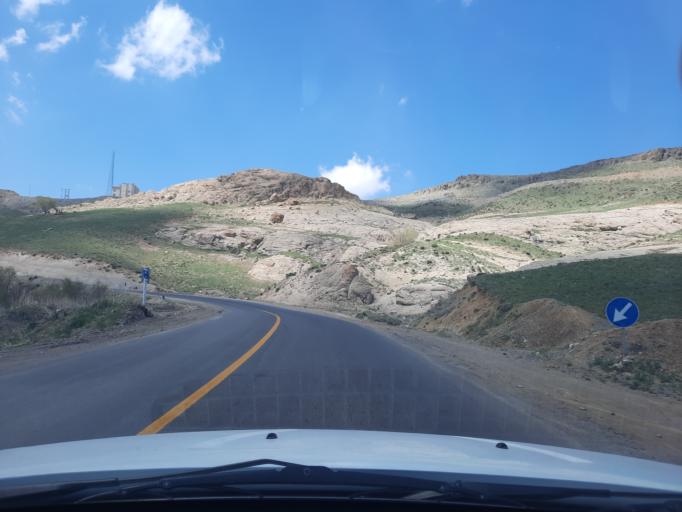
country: IR
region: Qazvin
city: Qazvin
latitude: 36.3811
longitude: 50.2090
